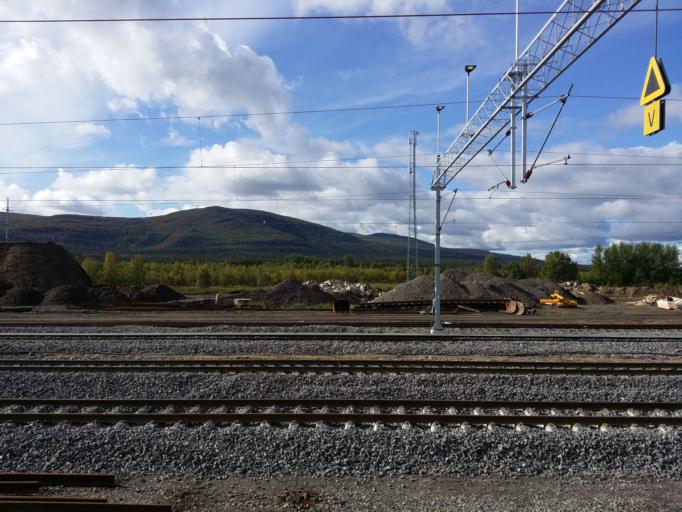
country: SE
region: Norrbotten
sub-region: Gallivare Kommun
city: Gaellivare
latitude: 67.1347
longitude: 20.6488
